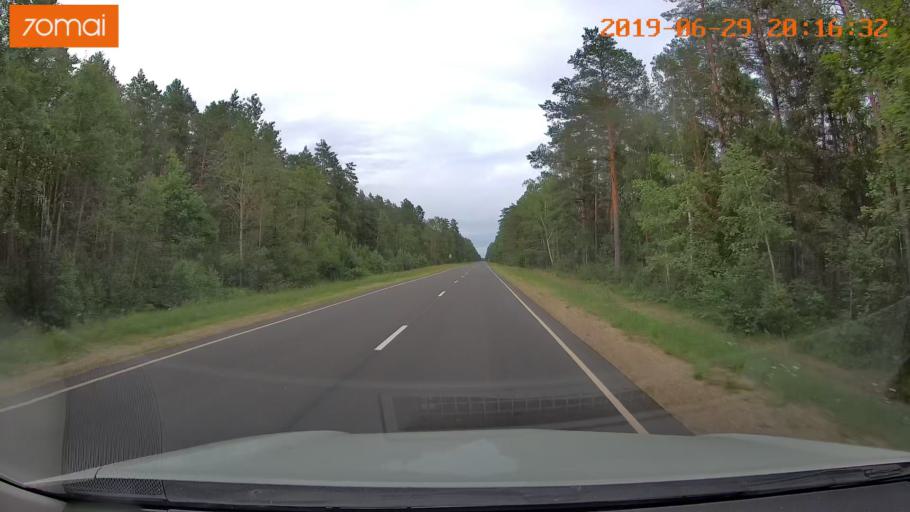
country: BY
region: Brest
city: Asnyezhytsy
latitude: 52.3819
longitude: 26.1981
